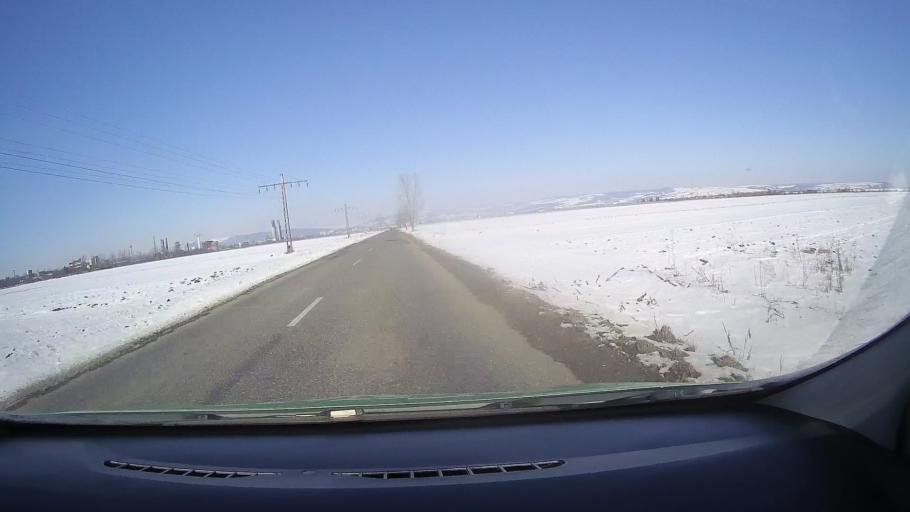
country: RO
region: Brasov
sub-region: Comuna Harseni
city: Harseni
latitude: 45.7989
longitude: 24.9935
